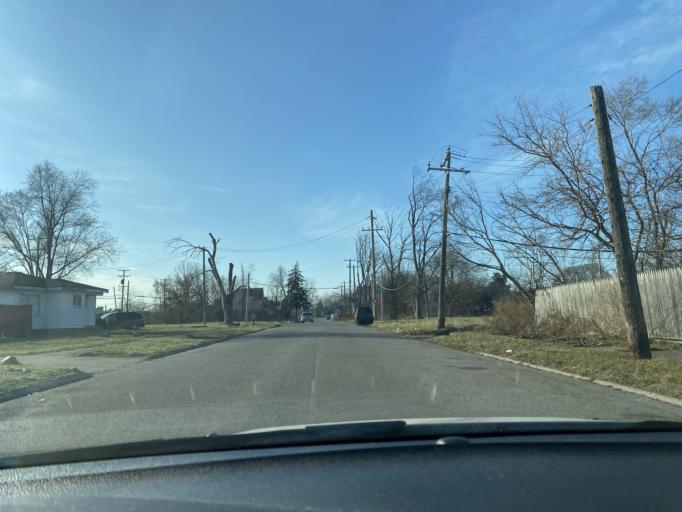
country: US
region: Michigan
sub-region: Wayne County
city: Grosse Pointe Park
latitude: 42.4086
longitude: -82.9537
